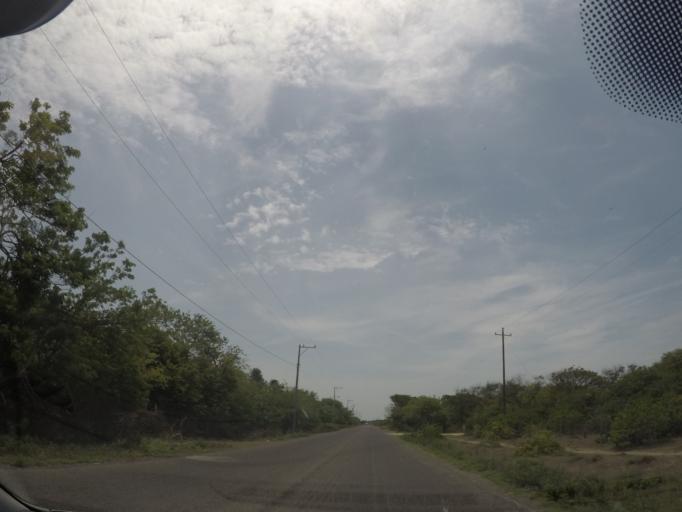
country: MX
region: Oaxaca
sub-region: San Mateo del Mar
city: Colonia Juarez
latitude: 16.2075
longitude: -95.0098
